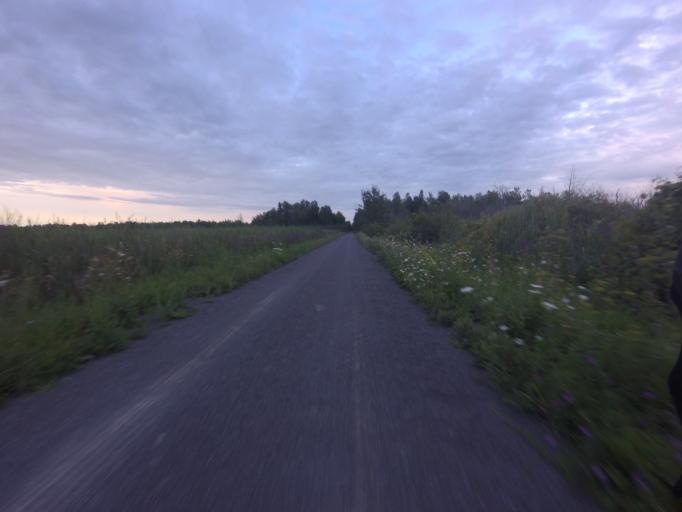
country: CA
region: Ontario
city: Carleton Place
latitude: 45.1871
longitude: -76.0334
